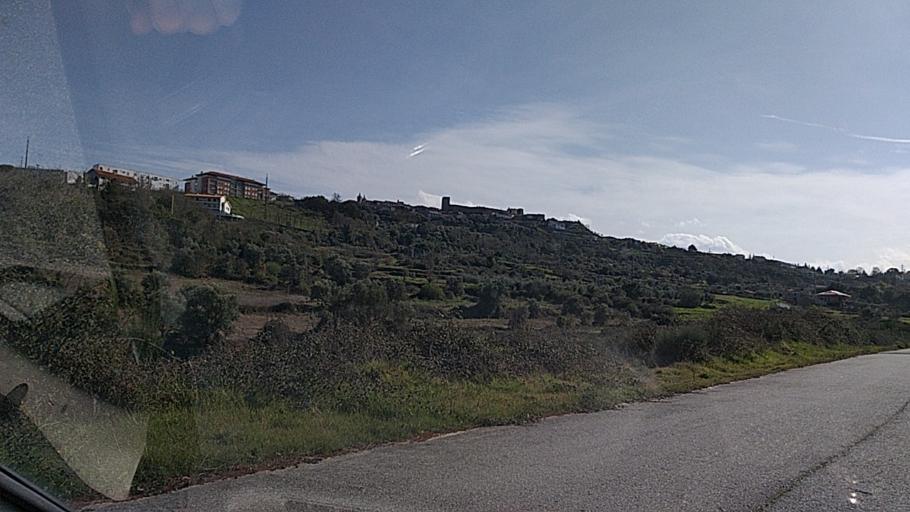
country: PT
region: Guarda
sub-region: Celorico da Beira
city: Celorico da Beira
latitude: 40.6442
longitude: -7.3956
